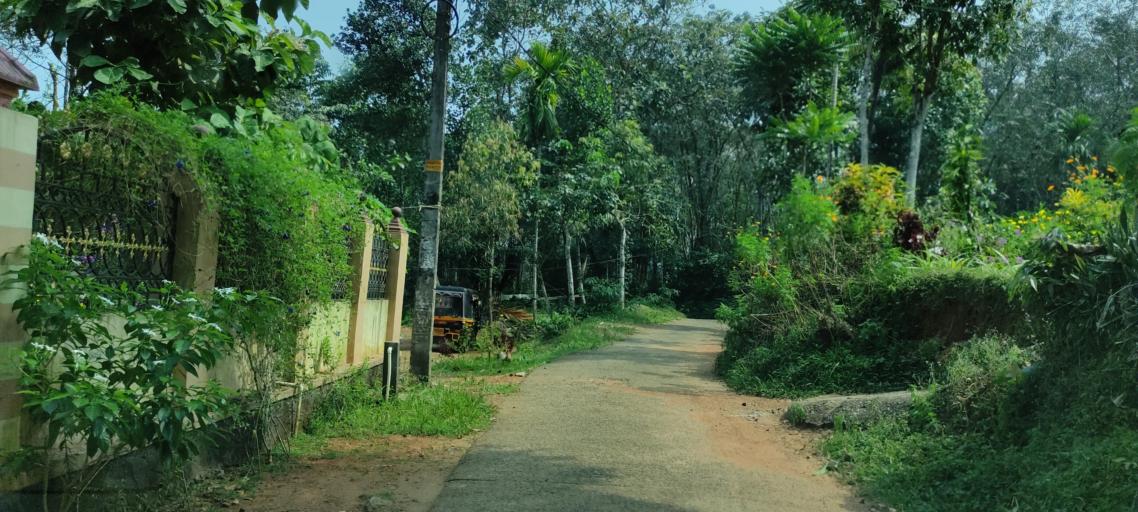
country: IN
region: Kerala
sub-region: Pattanamtitta
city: Adur
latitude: 9.2060
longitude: 76.6931
